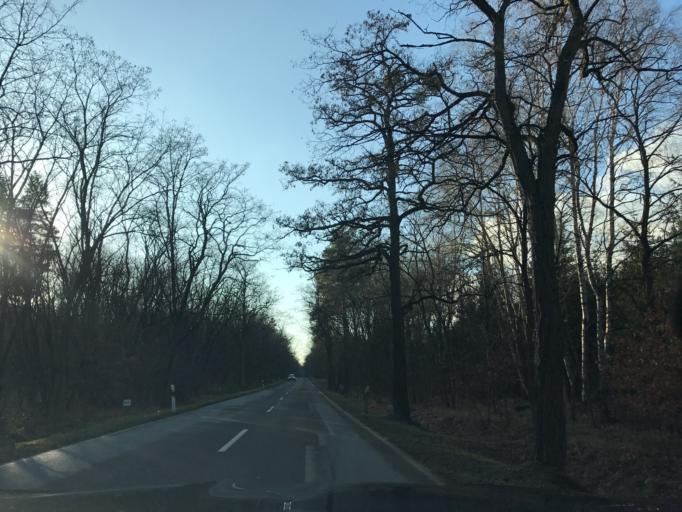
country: DE
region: Saxony-Anhalt
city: Mockern
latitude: 52.1686
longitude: 12.0118
